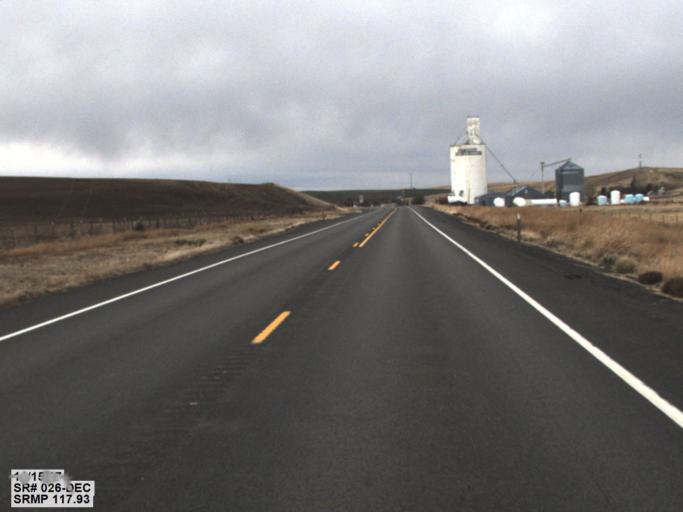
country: US
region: Washington
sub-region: Whitman County
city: Colfax
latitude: 46.8109
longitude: -117.6341
